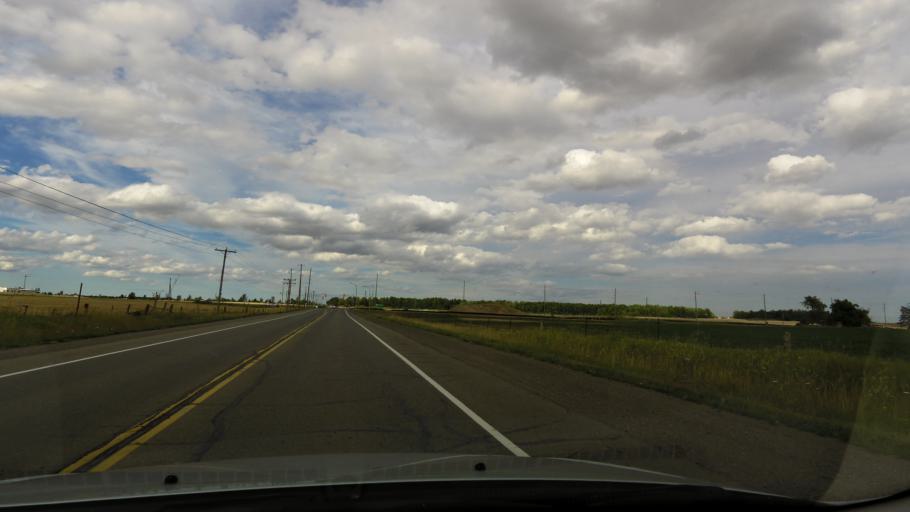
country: CA
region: Ontario
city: Brampton
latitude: 43.6929
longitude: -79.8692
